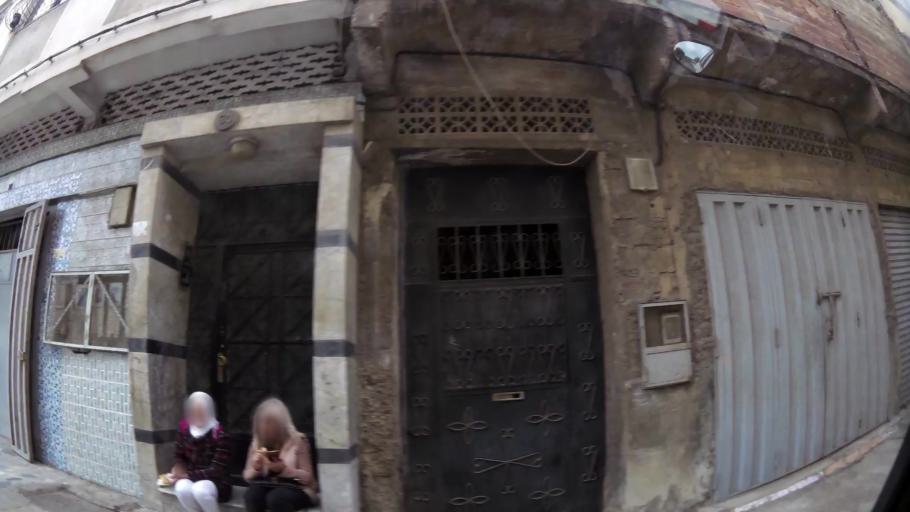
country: MA
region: Grand Casablanca
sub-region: Mediouna
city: Tit Mellil
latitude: 33.6118
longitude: -7.5113
